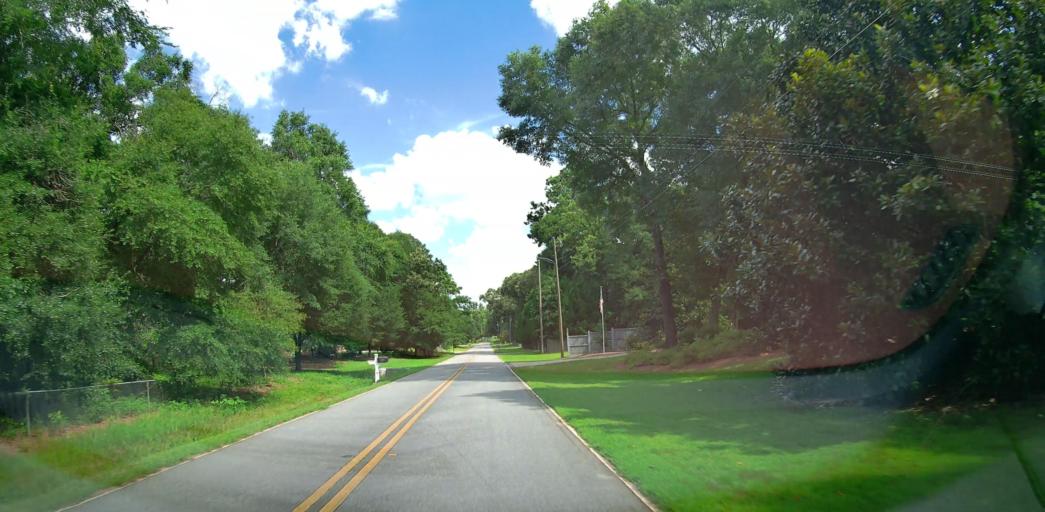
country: US
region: Georgia
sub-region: Houston County
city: Centerville
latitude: 32.5793
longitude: -83.6654
